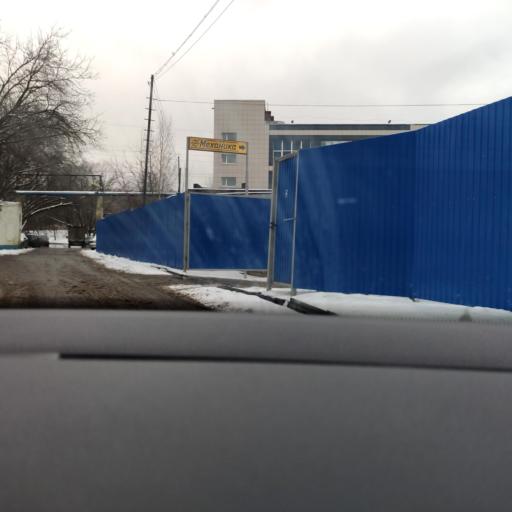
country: RU
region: Moscow
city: Metrogorodok
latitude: 55.8238
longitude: 37.7797
